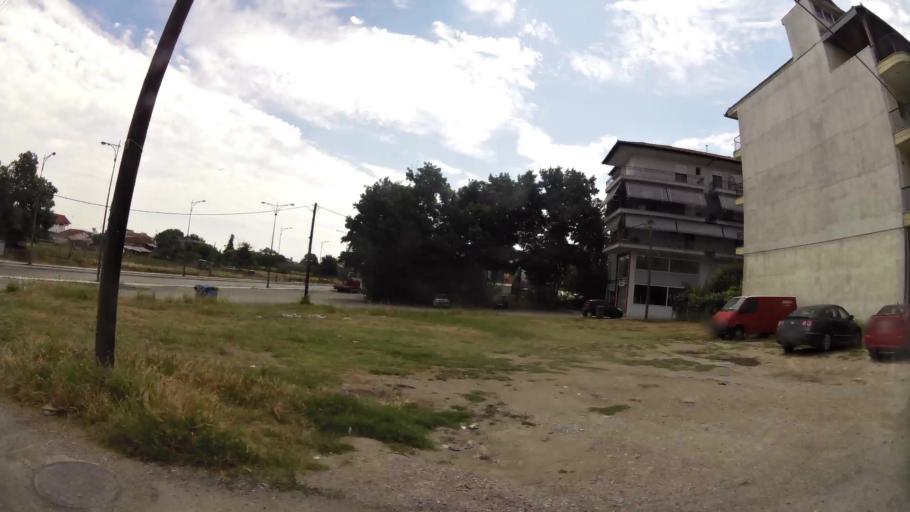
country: GR
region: Central Macedonia
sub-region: Nomos Pierias
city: Katerini
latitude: 40.2771
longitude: 22.5080
